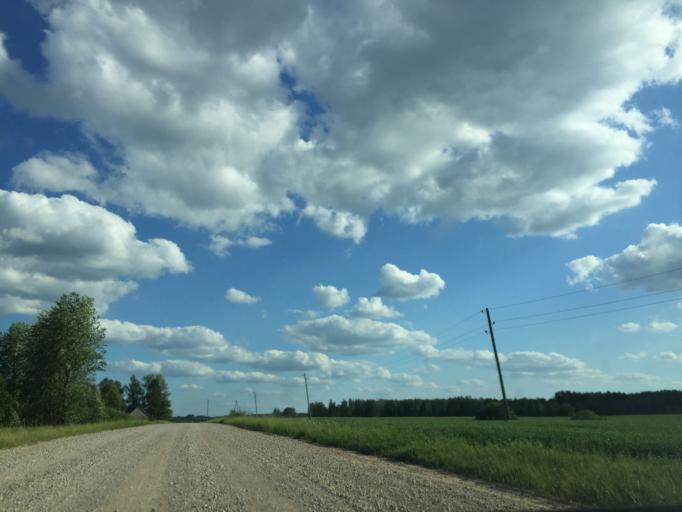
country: LV
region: Kandava
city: Kandava
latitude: 56.9112
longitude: 22.7919
